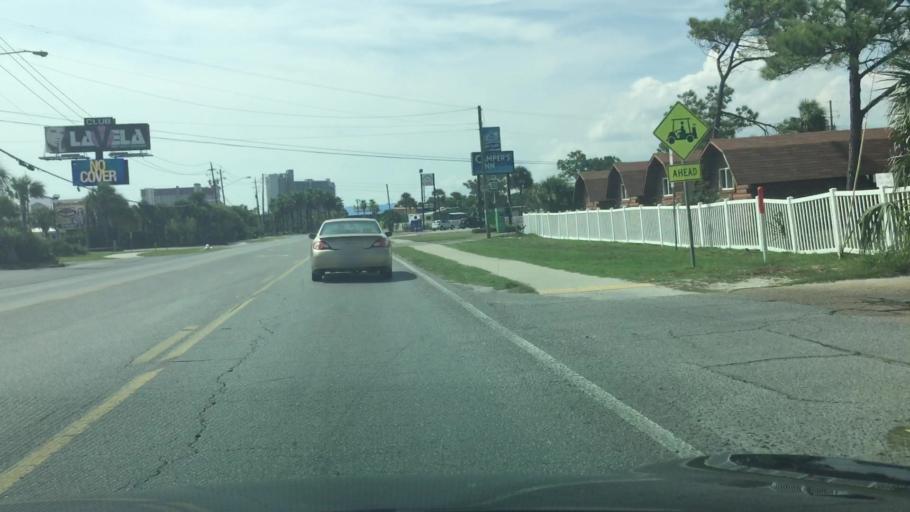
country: US
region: Florida
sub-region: Bay County
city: Panama City Beach
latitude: 30.1701
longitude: -85.7927
